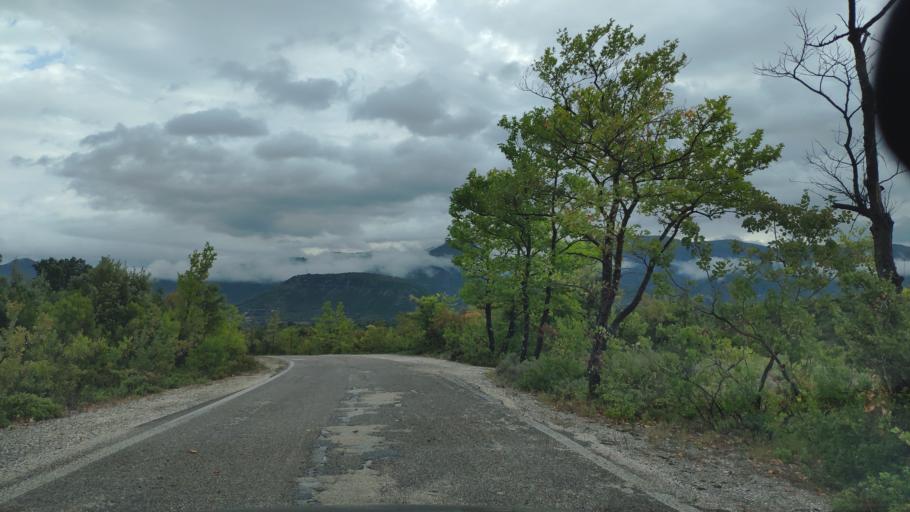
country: GR
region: West Greece
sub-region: Nomos Aitolias kai Akarnanias
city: Sardinia
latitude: 38.8455
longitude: 21.3231
